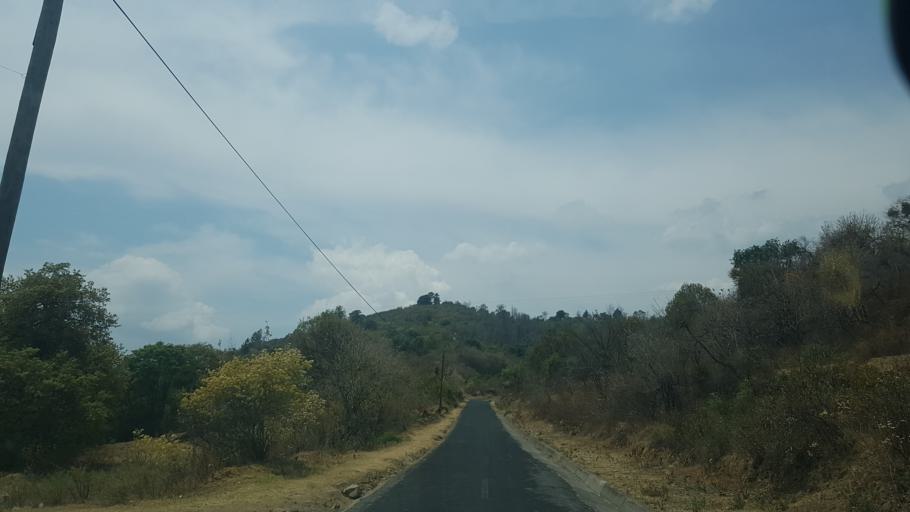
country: MX
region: Puebla
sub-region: Tochimilco
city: La Magdalena Yancuitlalpan
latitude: 18.8722
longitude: -98.6118
